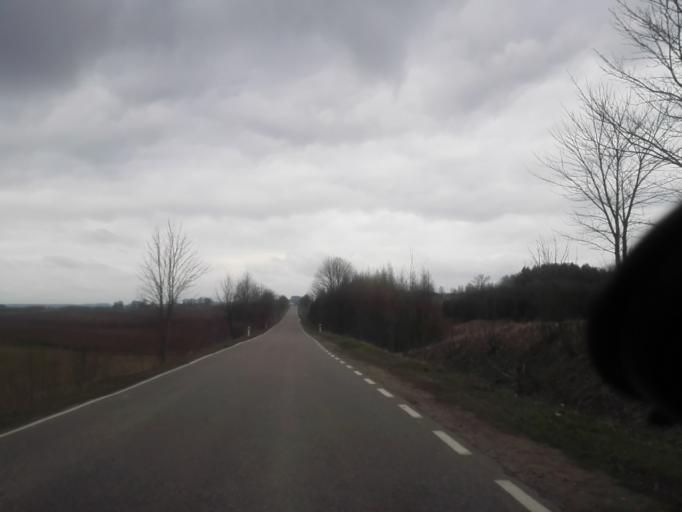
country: PL
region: Podlasie
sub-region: Suwalki
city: Suwalki
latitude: 54.2174
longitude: 22.9120
